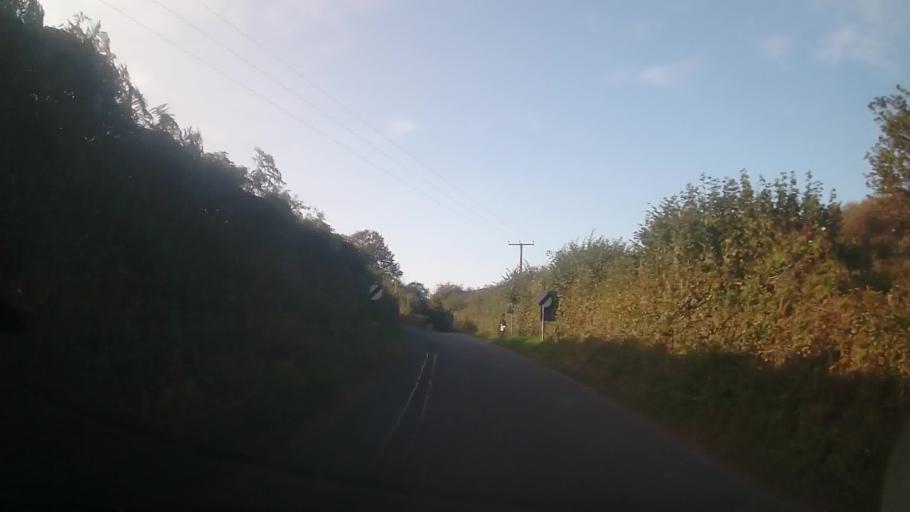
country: GB
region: Wales
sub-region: Pembrokeshire
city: Fishguard
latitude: 51.9805
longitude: -4.9337
